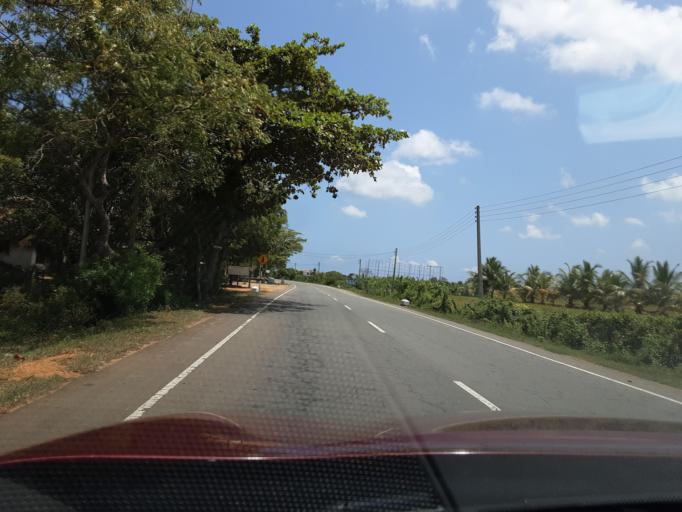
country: LK
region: Southern
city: Tangalla
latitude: 6.2412
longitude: 81.2268
